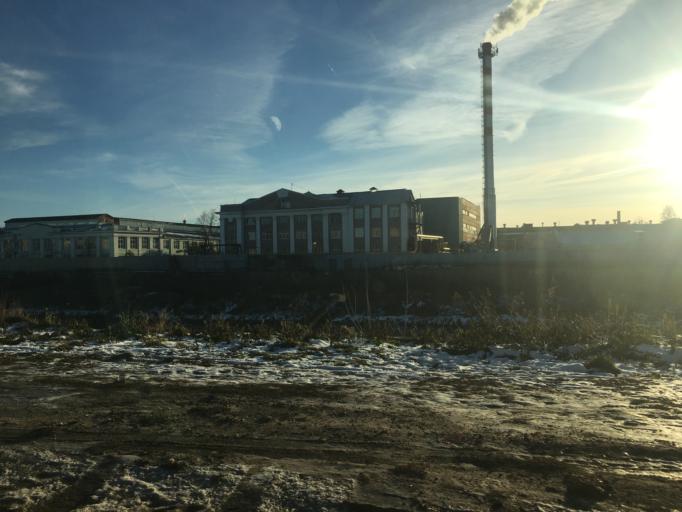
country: RU
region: Tula
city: Tula
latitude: 54.2054
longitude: 37.6086
